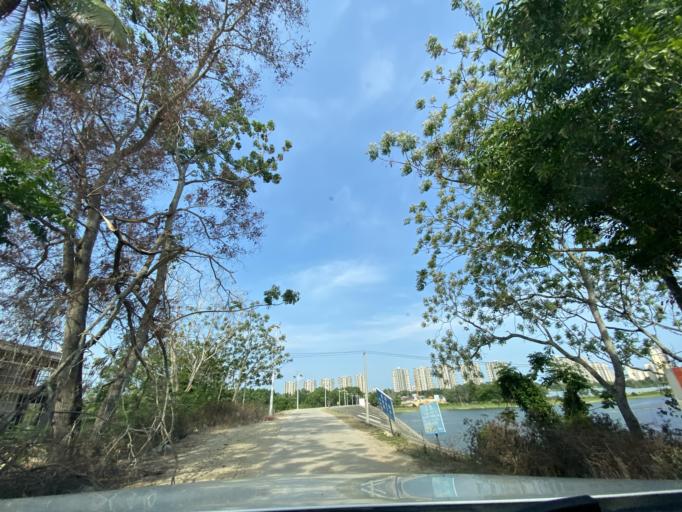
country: CN
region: Hainan
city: Yingzhou
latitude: 18.4069
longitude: 109.8328
